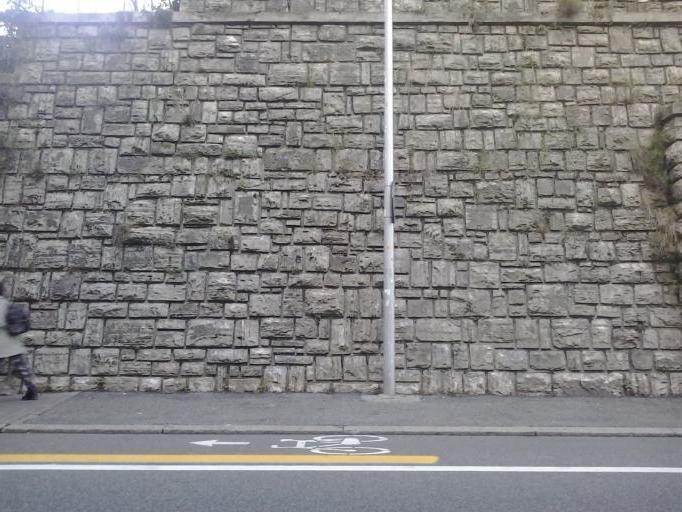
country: IT
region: Lombardy
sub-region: Provincia di Brescia
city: Brescia
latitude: 45.5444
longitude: 10.2244
